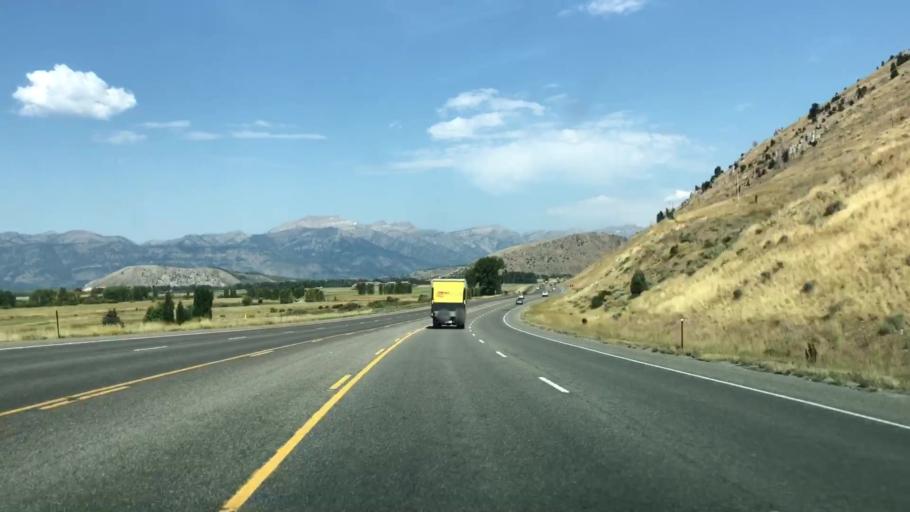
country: US
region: Wyoming
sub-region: Teton County
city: South Park
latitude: 43.4358
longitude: -110.7856
